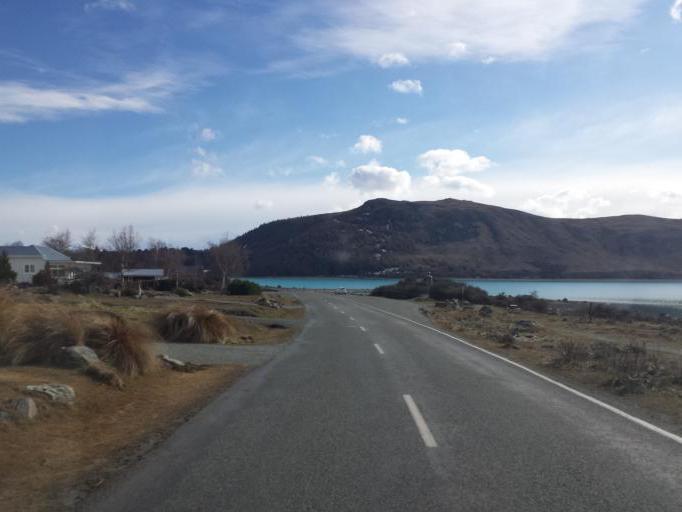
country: NZ
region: Canterbury
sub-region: Timaru District
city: Pleasant Point
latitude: -44.0043
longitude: 170.4849
